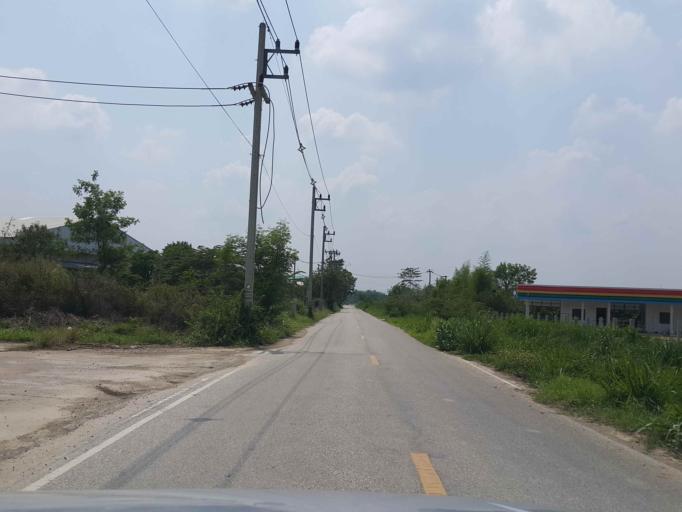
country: TH
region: Chiang Mai
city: Hang Dong
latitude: 18.7015
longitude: 98.9722
